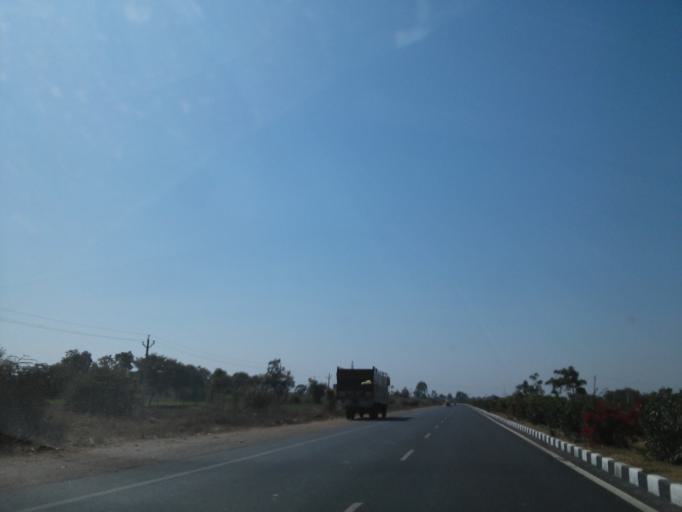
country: IN
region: Gujarat
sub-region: Sabar Kantha
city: Himatnagar
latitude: 23.5035
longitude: 72.9160
